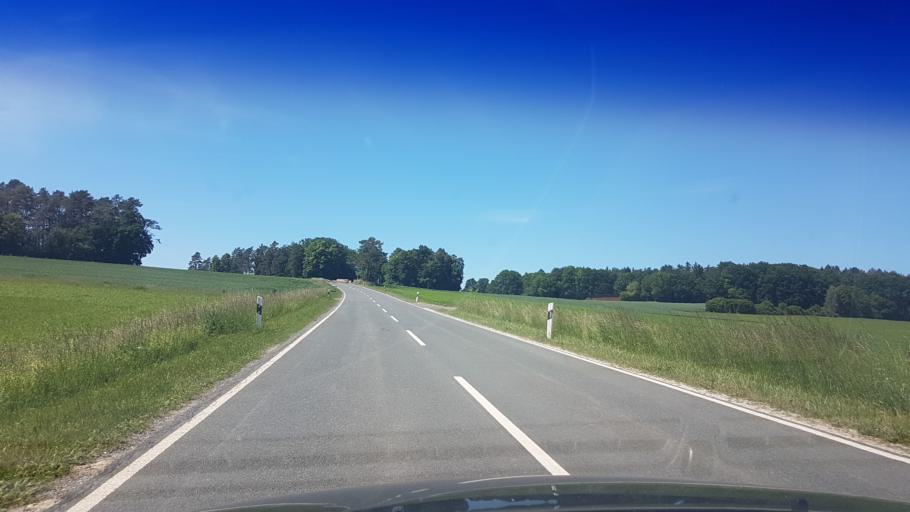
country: DE
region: Bavaria
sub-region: Upper Franconia
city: Weismain
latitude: 50.0398
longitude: 11.2569
